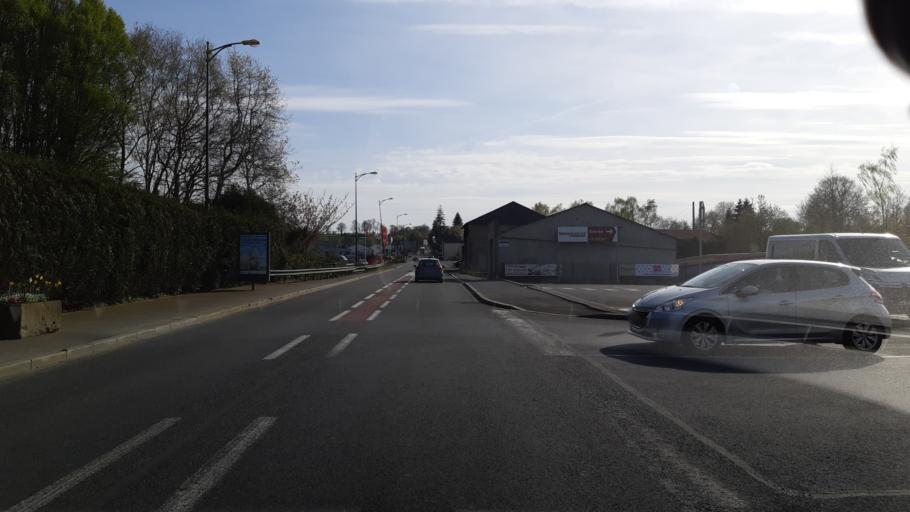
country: FR
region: Lower Normandy
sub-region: Departement de la Manche
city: Percy
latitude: 48.9138
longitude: -1.1933
